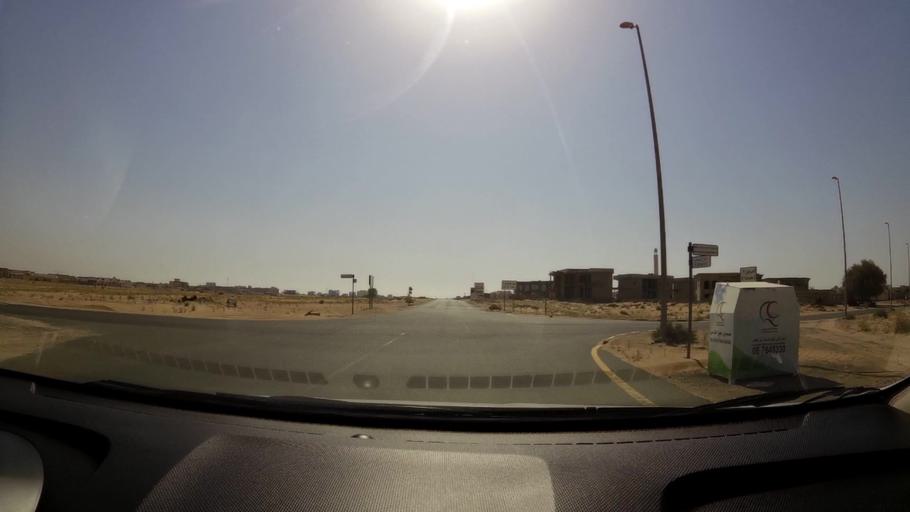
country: AE
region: Umm al Qaywayn
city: Umm al Qaywayn
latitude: 25.4812
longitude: 55.6036
